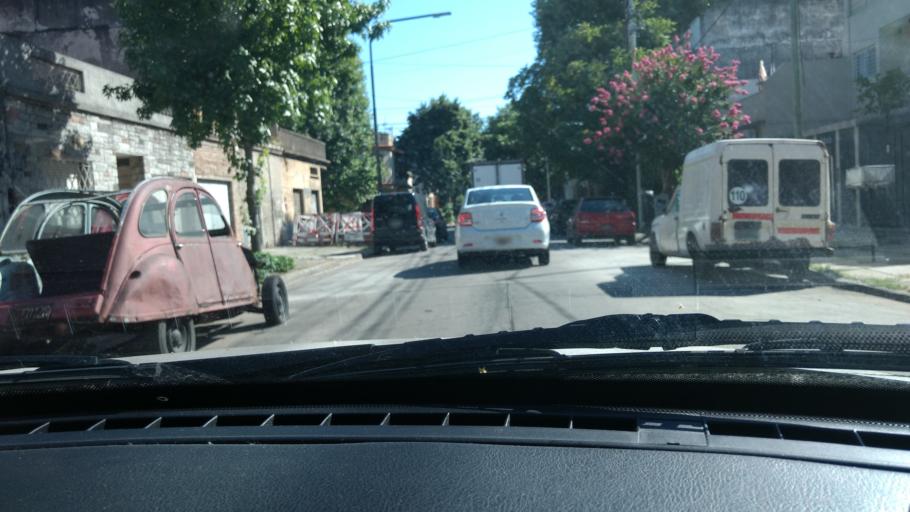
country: AR
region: Buenos Aires F.D.
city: Villa Santa Rita
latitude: -34.6188
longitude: -58.5169
